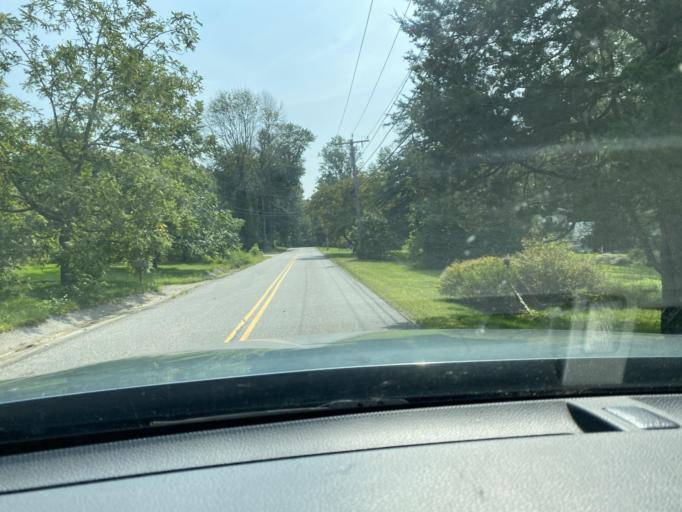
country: US
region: Connecticut
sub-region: New London County
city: Colchester
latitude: 41.6320
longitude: -72.2927
